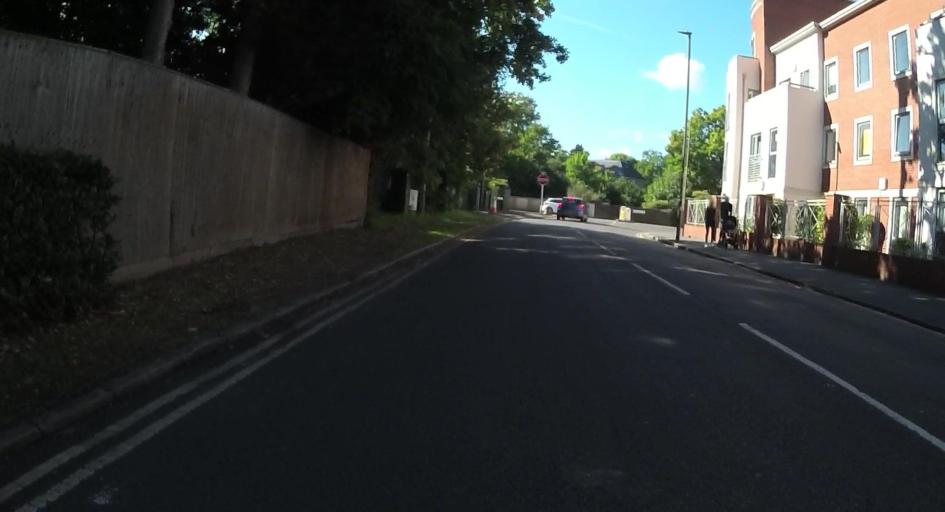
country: GB
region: England
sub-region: Surrey
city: Weybridge
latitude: 51.3671
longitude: -0.4427
